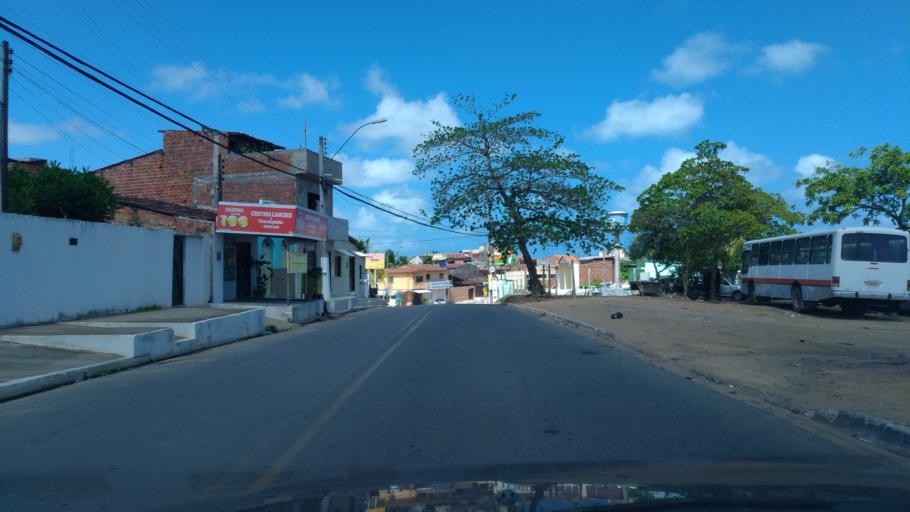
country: BR
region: Alagoas
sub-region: Maceio
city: Maceio
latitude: -9.6175
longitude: -35.7045
